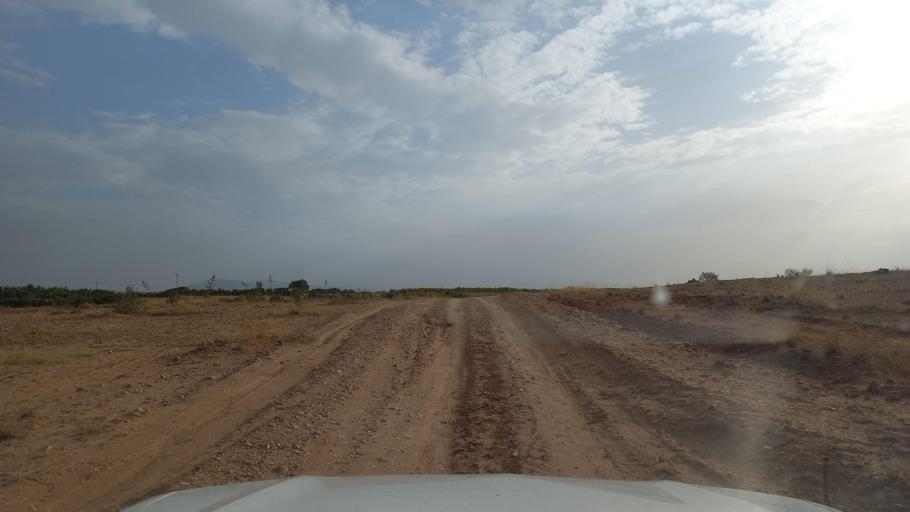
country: TN
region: Al Qasrayn
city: Kasserine
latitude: 35.2885
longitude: 9.0453
